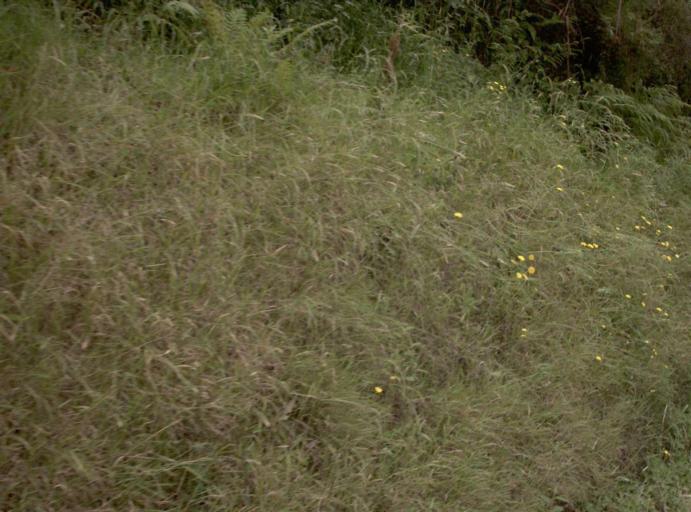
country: AU
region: Victoria
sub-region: Yarra Ranges
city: Healesville
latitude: -37.6051
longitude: 145.6169
